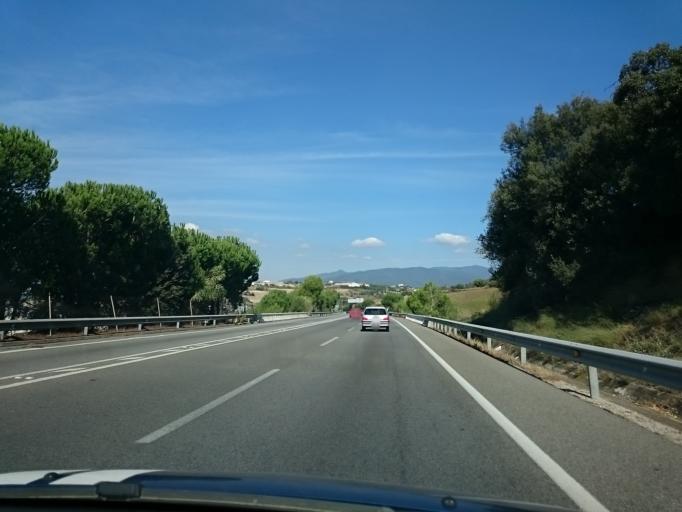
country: ES
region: Catalonia
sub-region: Provincia de Barcelona
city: Les Franqueses del Valles
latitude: 41.6084
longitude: 2.3094
